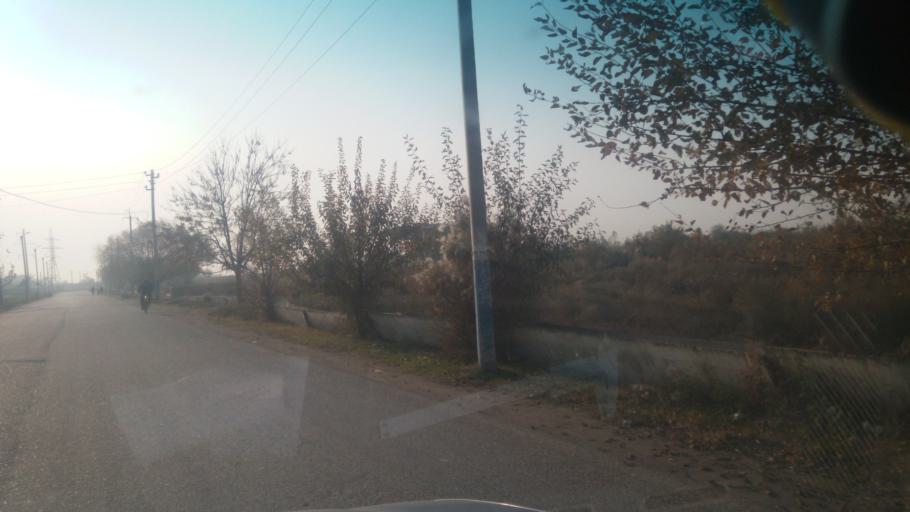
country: UZ
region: Sirdaryo
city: Guliston
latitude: 40.5169
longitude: 68.7745
